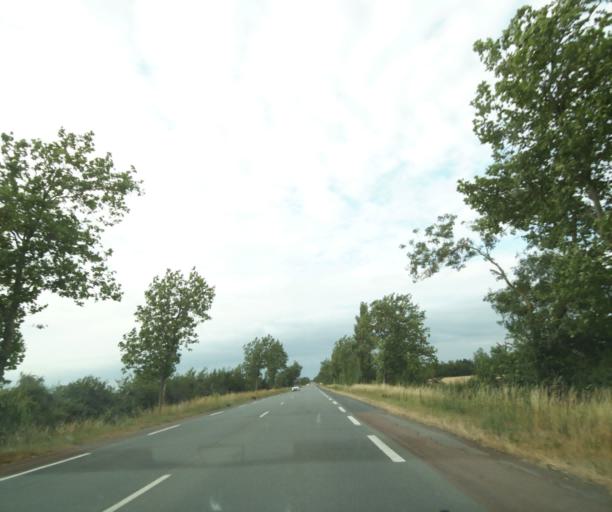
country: FR
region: Poitou-Charentes
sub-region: Departement de la Charente-Maritime
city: Marans
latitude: 46.2876
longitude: -0.9930
